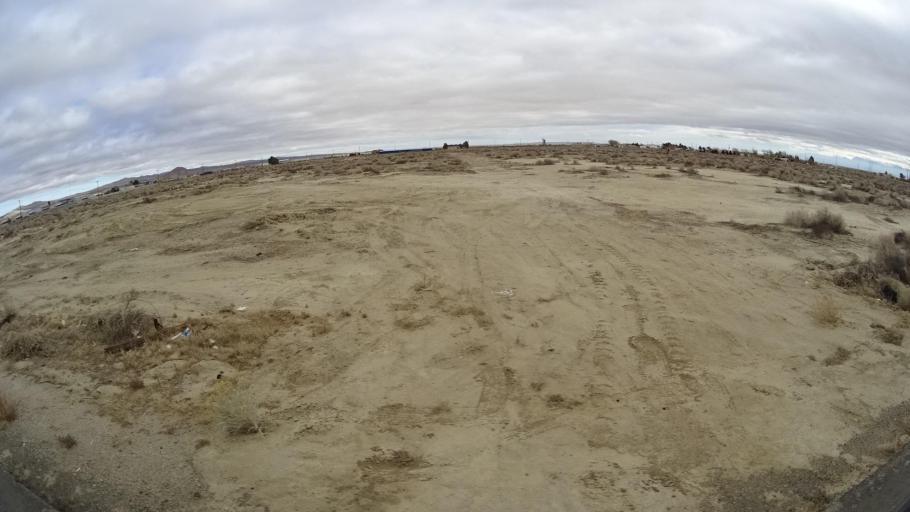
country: US
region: California
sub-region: Kern County
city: Rosamond
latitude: 34.8406
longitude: -118.1670
